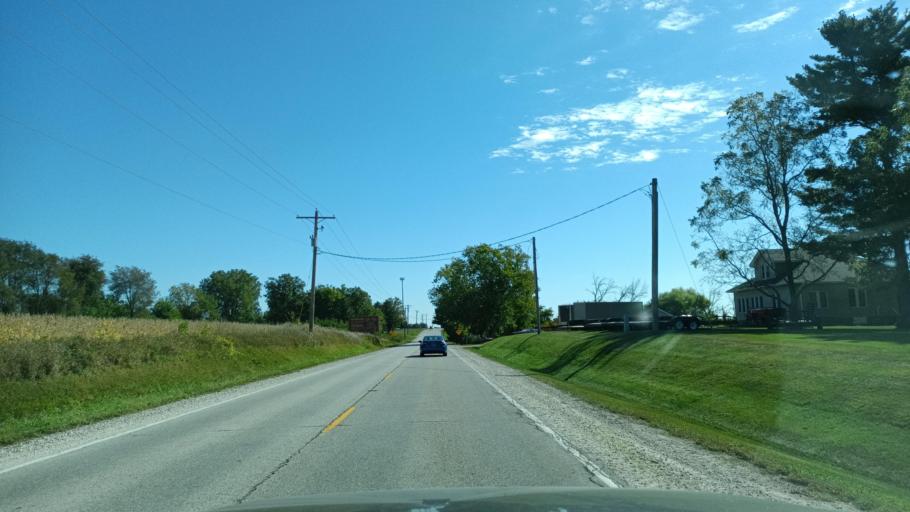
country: US
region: Illinois
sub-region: Knox County
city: Knoxville
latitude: 40.9079
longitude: -90.2647
